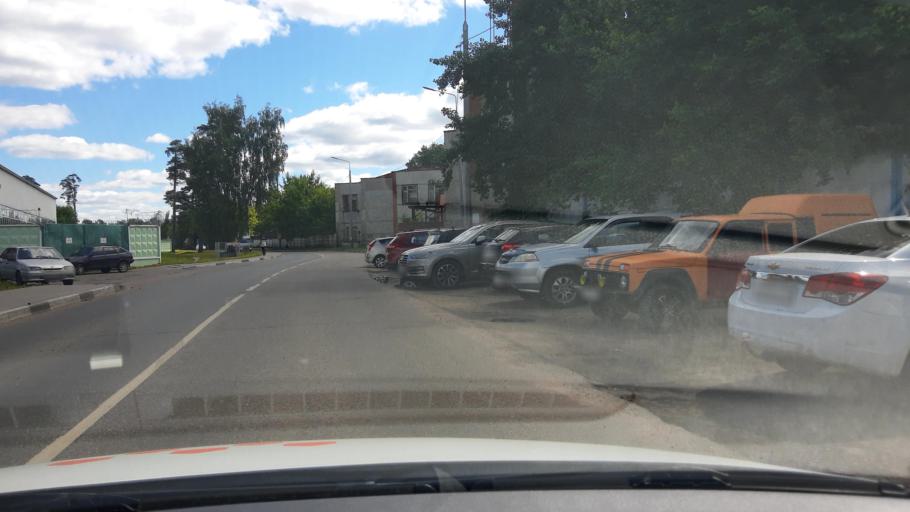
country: RU
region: Moskovskaya
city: Noginsk
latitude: 55.8770
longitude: 38.4460
